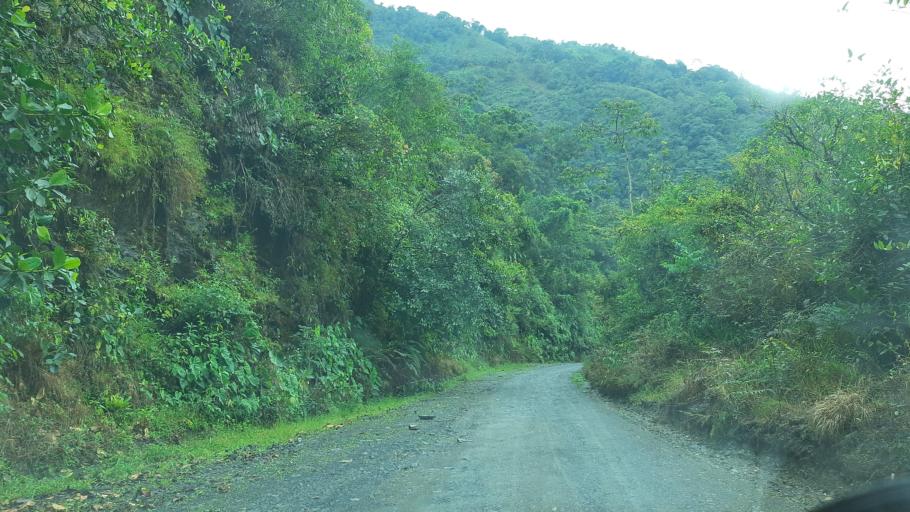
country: CO
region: Boyaca
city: Chivor
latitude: 4.9124
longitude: -73.3065
